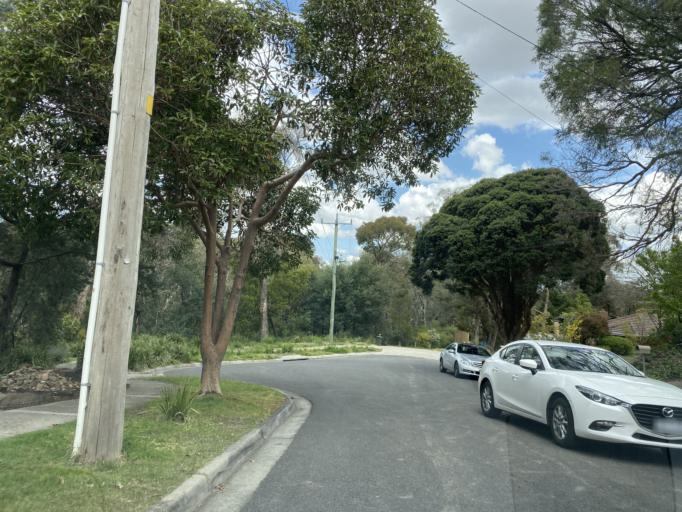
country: AU
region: Victoria
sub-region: Whitehorse
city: Burwood
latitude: -37.8617
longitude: 145.1291
